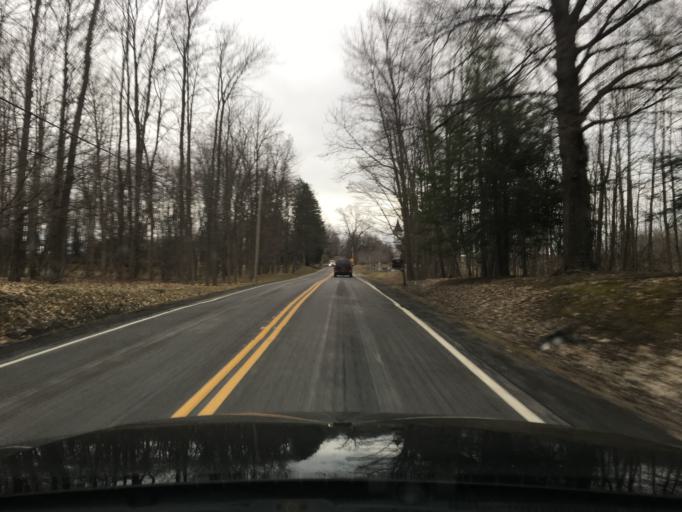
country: US
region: New York
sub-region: Ontario County
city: Victor
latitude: 43.0457
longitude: -77.3857
